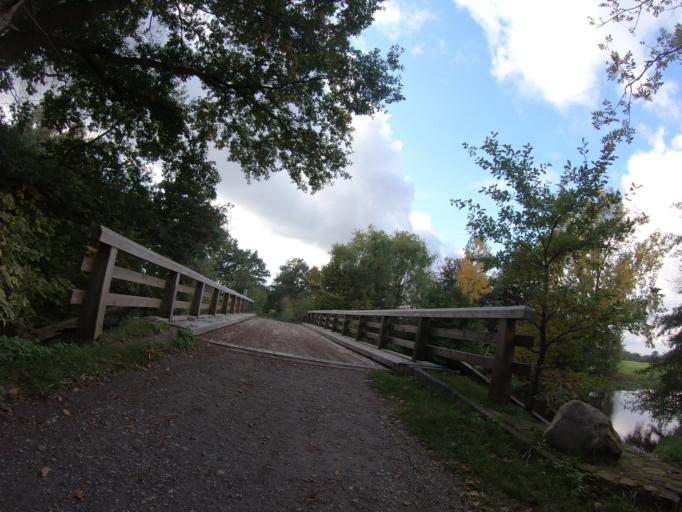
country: DE
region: Lower Saxony
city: Gifhorn
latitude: 52.5072
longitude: 10.5544
